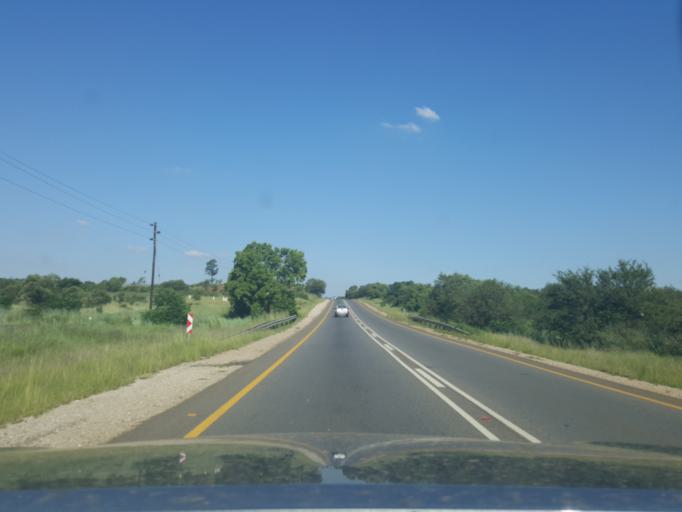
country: ZA
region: Gauteng
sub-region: City of Tshwane Metropolitan Municipality
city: Cullinan
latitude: -25.7540
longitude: 28.3941
